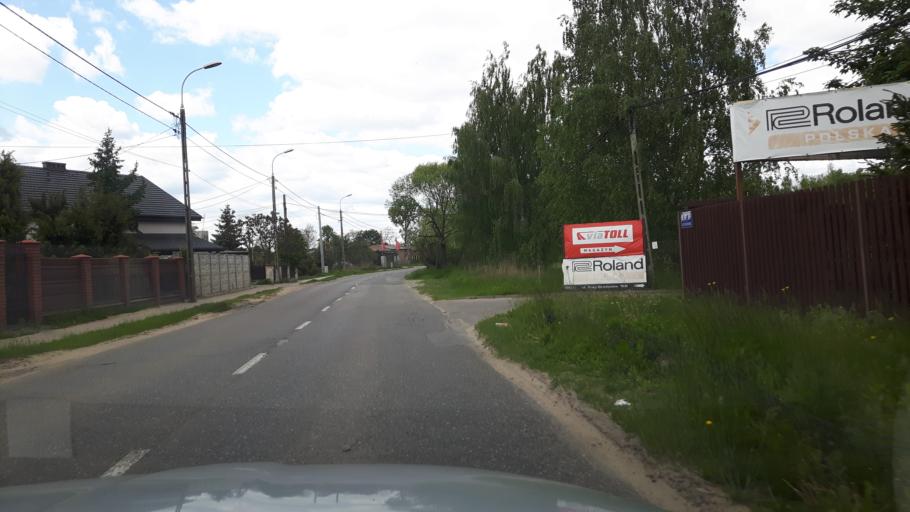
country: PL
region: Masovian Voivodeship
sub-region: Warszawa
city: Targowek
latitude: 52.3263
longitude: 21.0622
